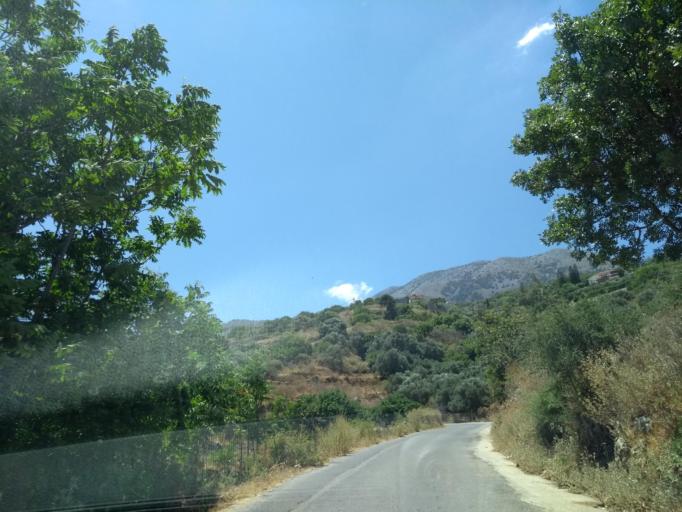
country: GR
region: Crete
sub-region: Nomos Chanias
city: Georgioupolis
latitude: 35.3174
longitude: 24.2907
